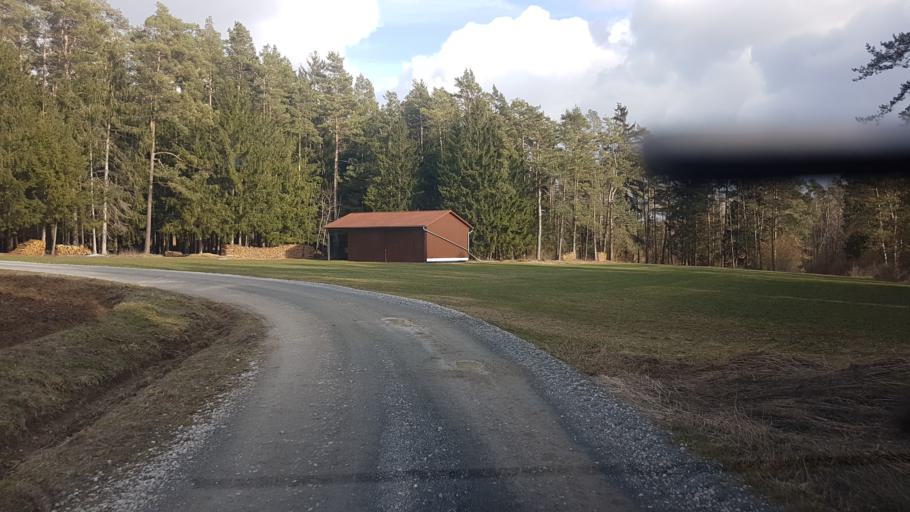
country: DE
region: Bavaria
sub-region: Upper Franconia
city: Stadelhofen
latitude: 50.0004
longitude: 11.2317
